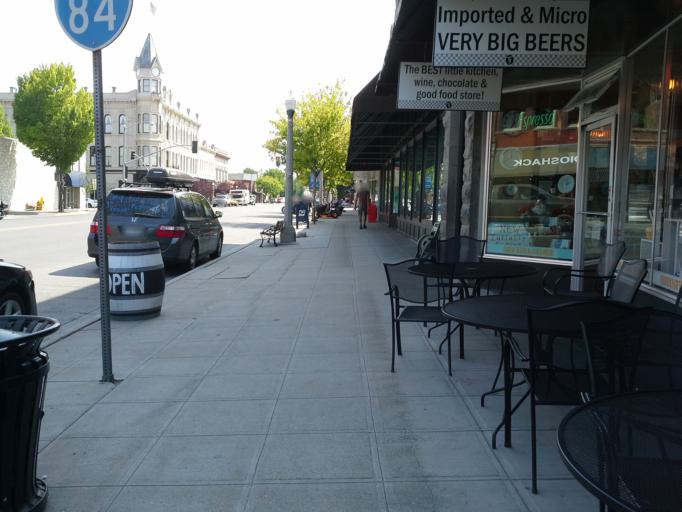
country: US
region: Oregon
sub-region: Baker County
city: Baker City
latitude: 44.7779
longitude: -117.8299
